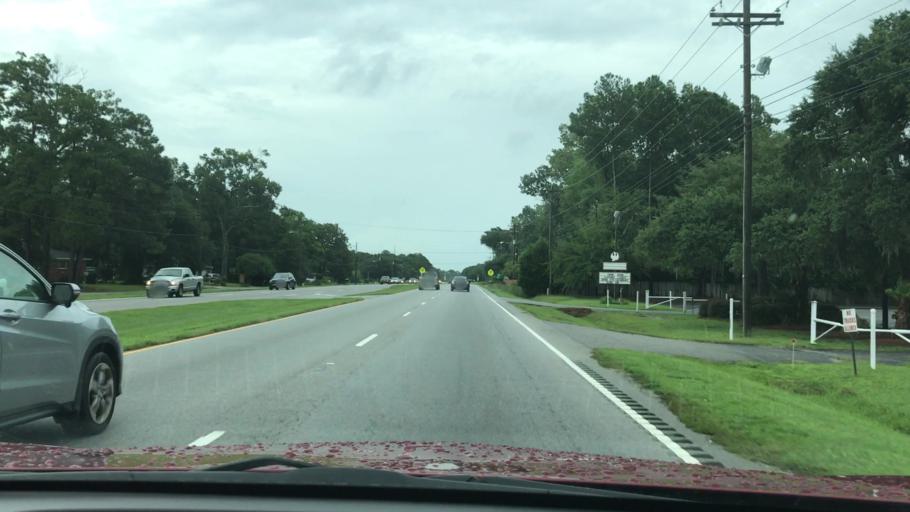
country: US
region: South Carolina
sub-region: Charleston County
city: Shell Point
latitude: 32.7960
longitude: -80.0766
